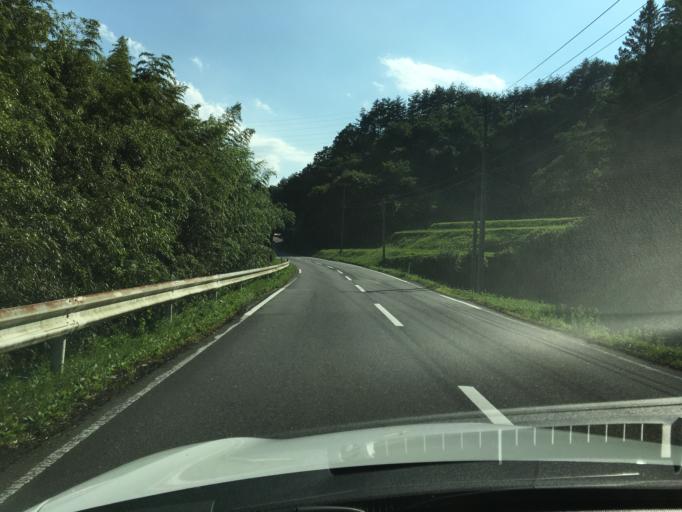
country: JP
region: Fukushima
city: Ishikawa
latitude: 37.2026
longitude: 140.5115
